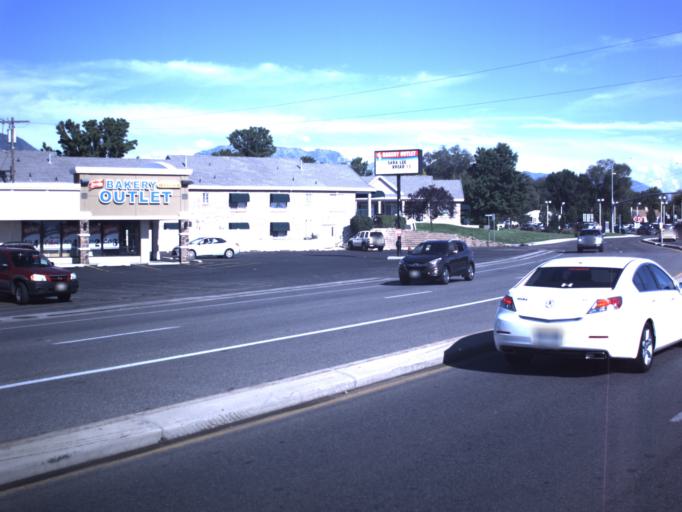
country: US
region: Utah
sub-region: Utah County
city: American Fork
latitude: 40.3781
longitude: -111.8129
